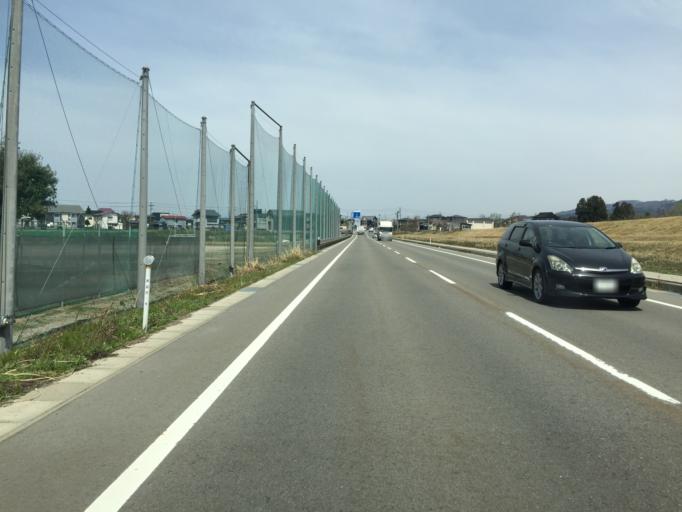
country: JP
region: Niigata
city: Ojiya
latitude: 37.3276
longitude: 138.8100
